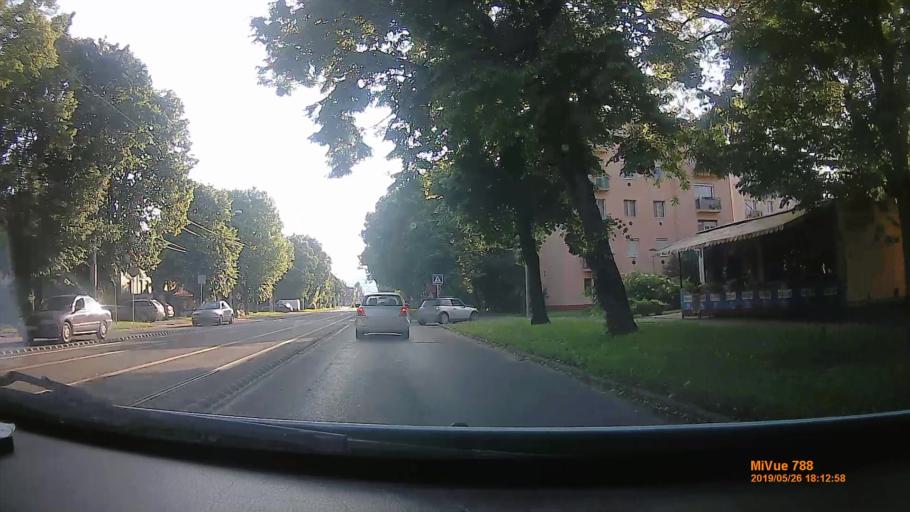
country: HU
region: Borsod-Abauj-Zemplen
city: Miskolc
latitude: 48.1025
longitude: 20.7407
